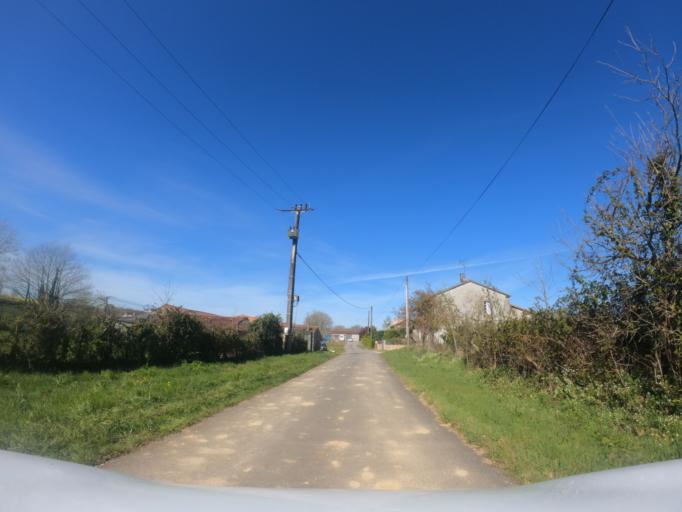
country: FR
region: Pays de la Loire
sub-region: Departement de la Vendee
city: Saint-Pierre-du-Chemin
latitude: 46.6952
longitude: -0.7101
